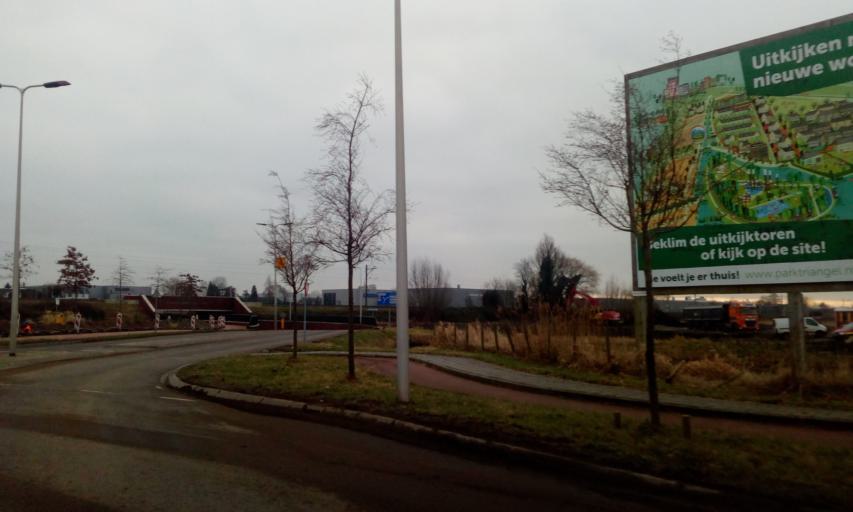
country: NL
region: South Holland
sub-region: Gemeente Waddinxveen
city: Waddinxveen
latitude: 52.0367
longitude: 4.6478
